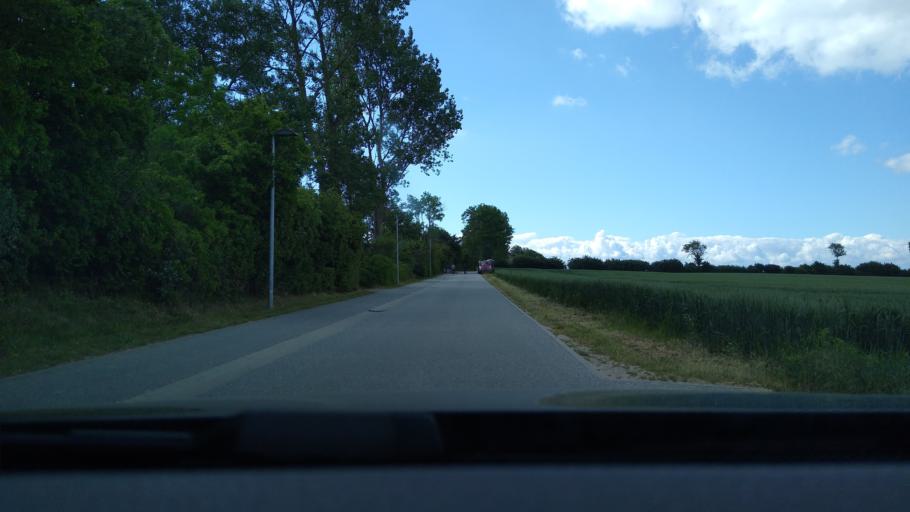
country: DE
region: Schleswig-Holstein
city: Dahme
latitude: 54.2127
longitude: 11.0894
